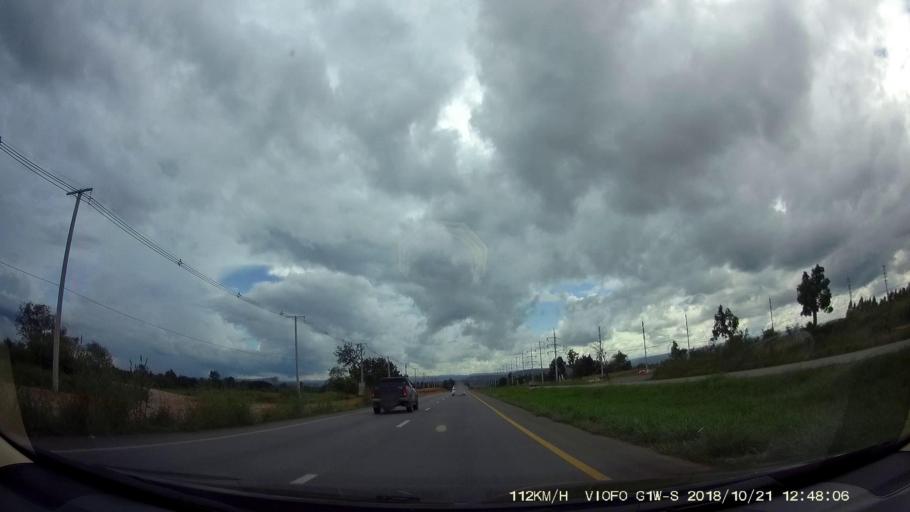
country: TH
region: Nakhon Ratchasima
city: Amphoe Sikhiu
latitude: 14.9179
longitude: 101.6840
